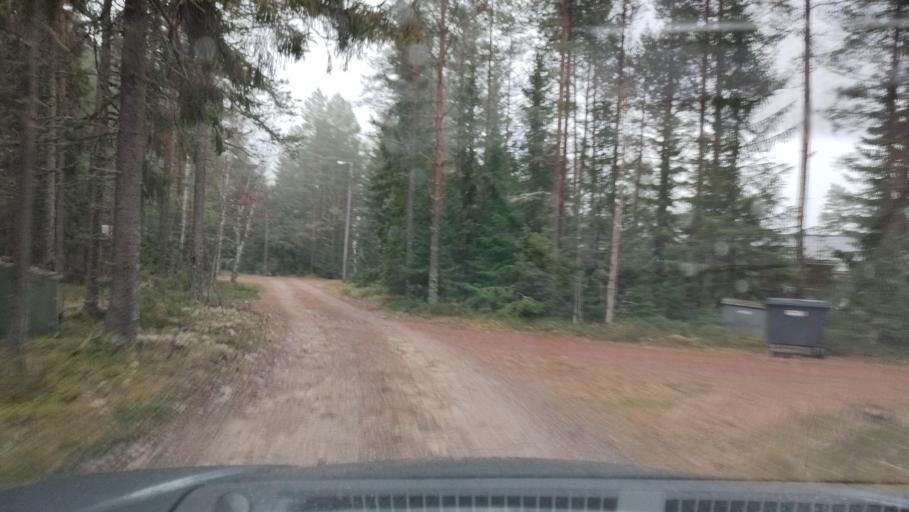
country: FI
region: Southern Ostrobothnia
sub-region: Suupohja
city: Karijoki
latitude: 62.1967
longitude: 21.7835
